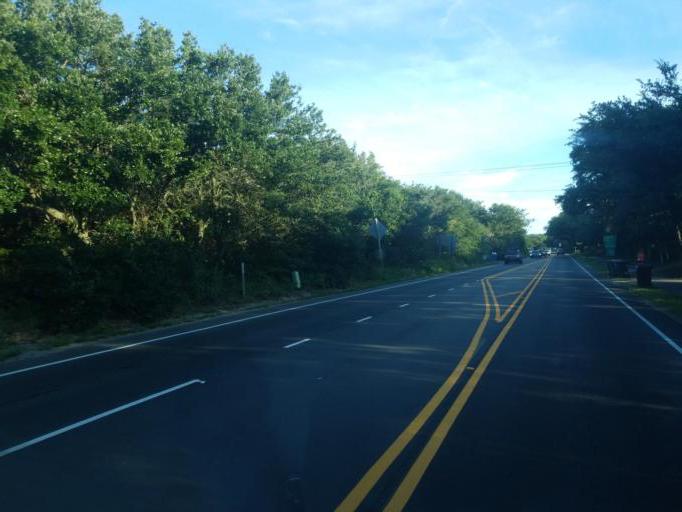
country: US
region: North Carolina
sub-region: Dare County
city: Southern Shores
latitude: 36.1506
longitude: -75.7419
